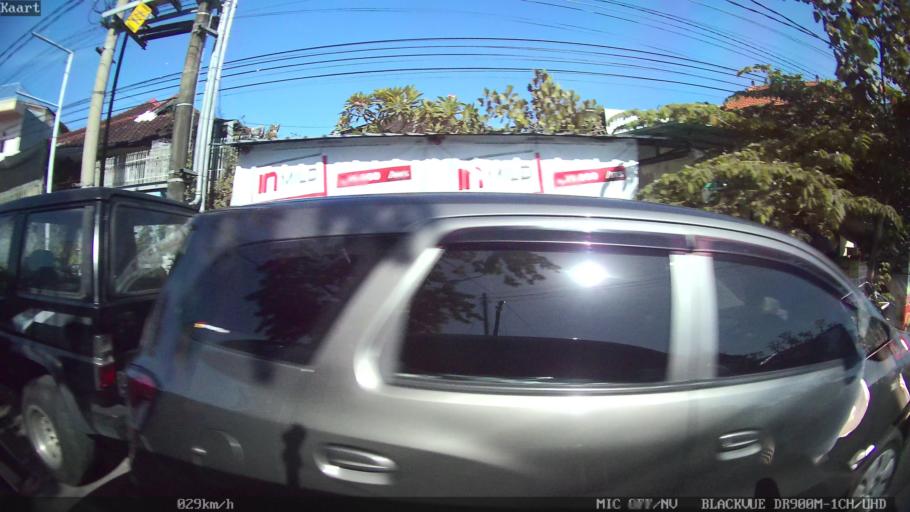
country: ID
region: Bali
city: Banjar Karangsuling
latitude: -8.6173
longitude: 115.1905
